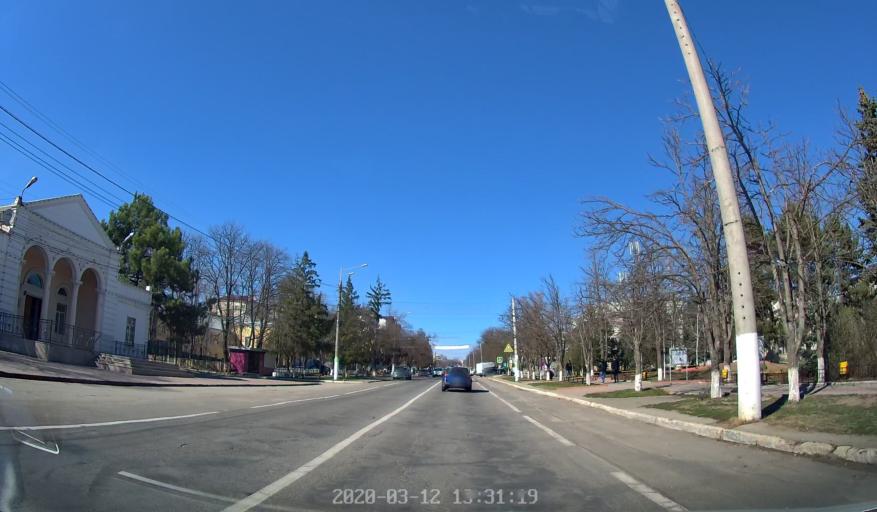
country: MD
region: Laloveni
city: Ialoveni
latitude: 46.9461
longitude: 28.7753
